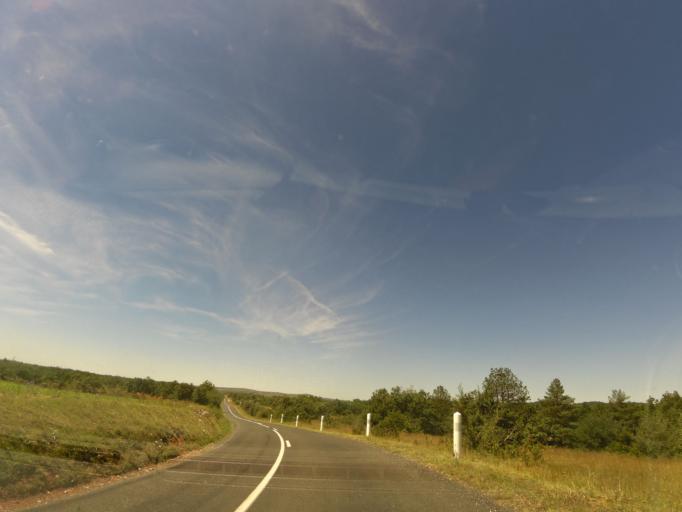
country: FR
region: Midi-Pyrenees
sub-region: Departement de l'Aveyron
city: La Cavalerie
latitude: 43.9555
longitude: 3.2368
